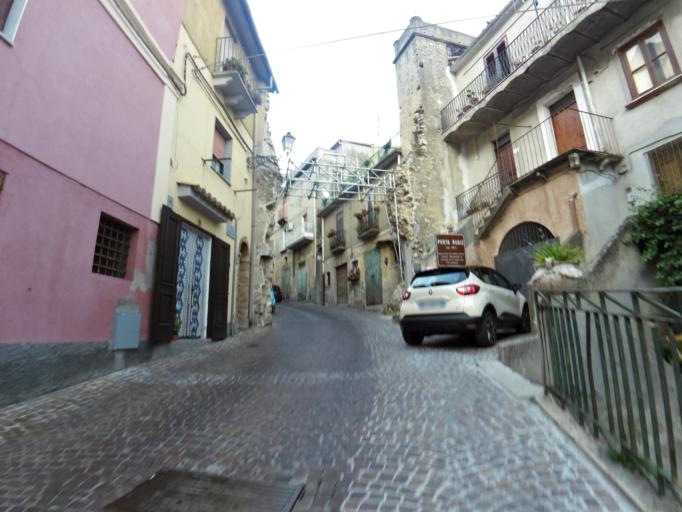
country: IT
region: Calabria
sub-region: Provincia di Reggio Calabria
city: Stilo
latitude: 38.4783
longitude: 16.4687
